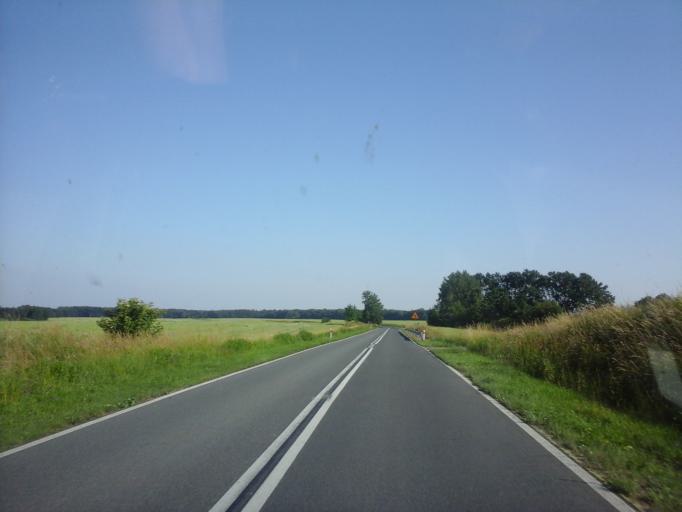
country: PL
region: West Pomeranian Voivodeship
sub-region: Powiat stargardzki
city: Chociwel
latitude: 53.5227
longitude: 15.3158
